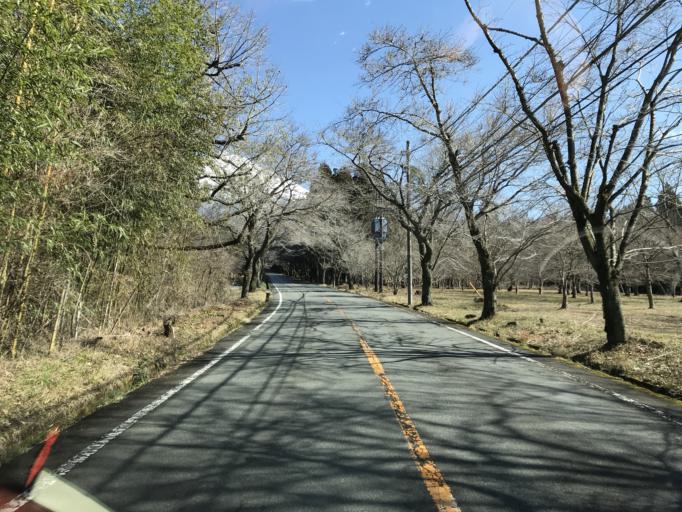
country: JP
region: Shizuoka
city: Fujinomiya
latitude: 35.2791
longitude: 138.6593
